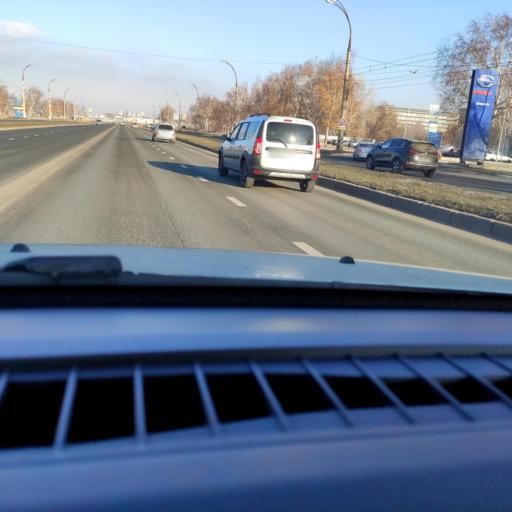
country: RU
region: Samara
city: Tol'yatti
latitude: 53.5482
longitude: 49.2659
